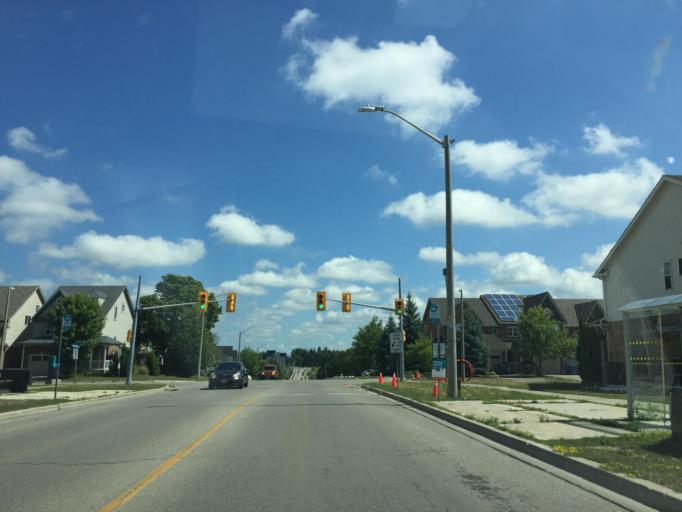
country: CA
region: Ontario
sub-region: Wellington County
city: Guelph
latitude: 43.5114
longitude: -80.2095
